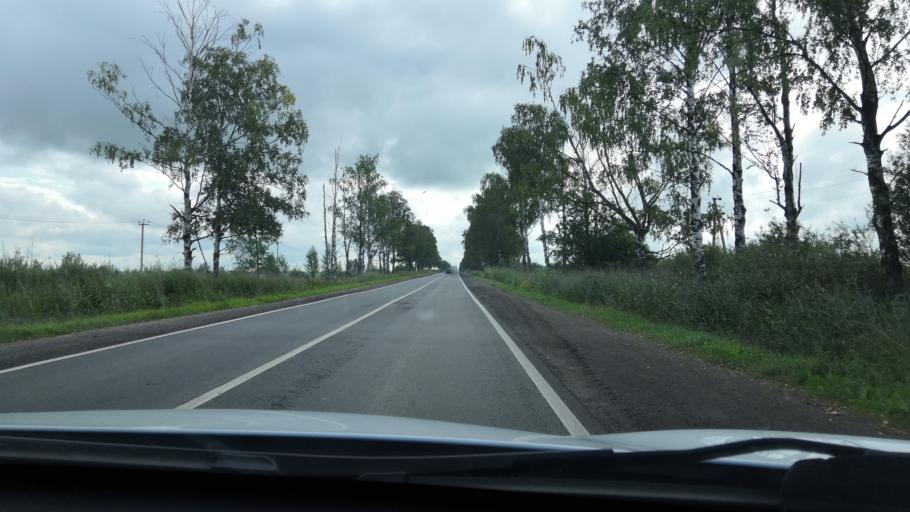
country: RU
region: St.-Petersburg
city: Tyarlevo
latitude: 59.7104
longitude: 30.4806
